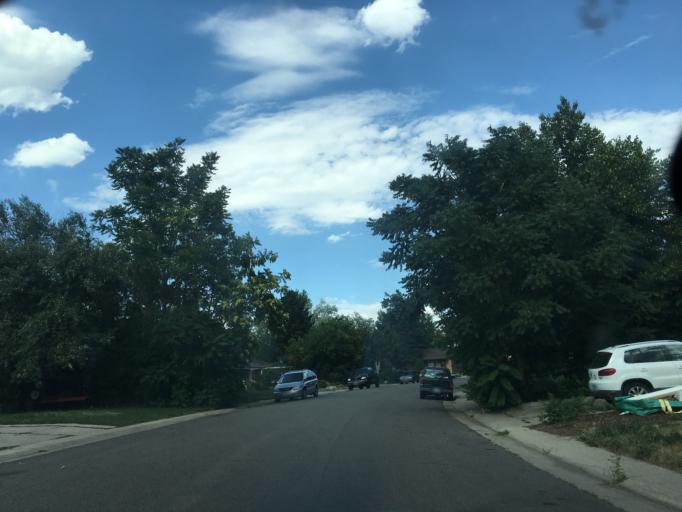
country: US
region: Colorado
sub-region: Arapahoe County
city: Sheridan
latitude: 39.6878
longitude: -105.0355
